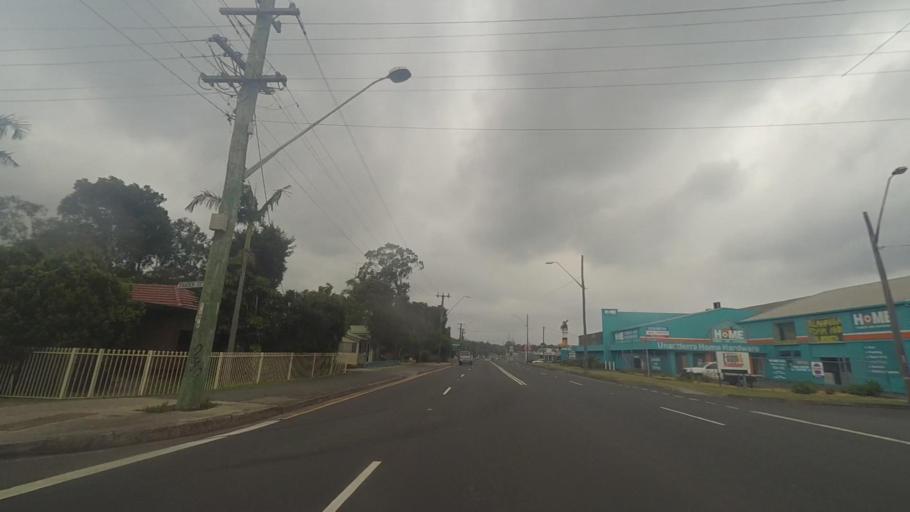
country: AU
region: New South Wales
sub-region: Wollongong
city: Cordeaux Heights
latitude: -34.4519
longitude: 150.8474
